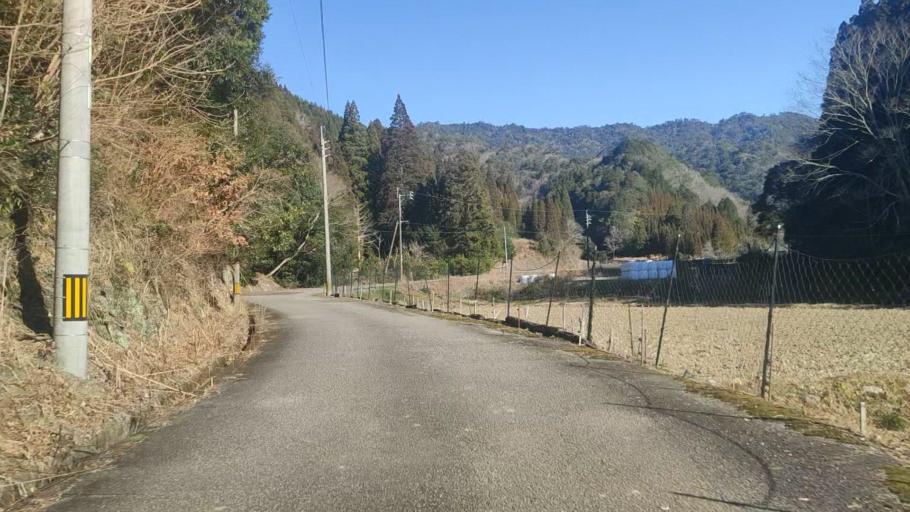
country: JP
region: Oita
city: Saiki
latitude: 32.7777
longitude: 131.8302
